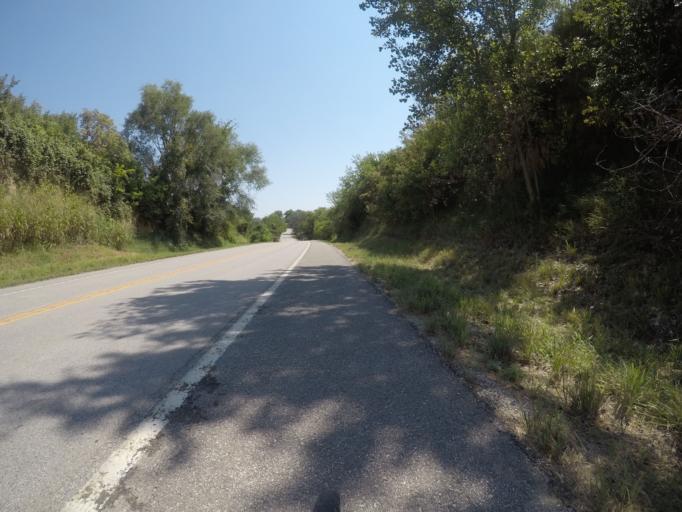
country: US
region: Missouri
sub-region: Platte County
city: Weston
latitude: 39.4352
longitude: -94.9209
